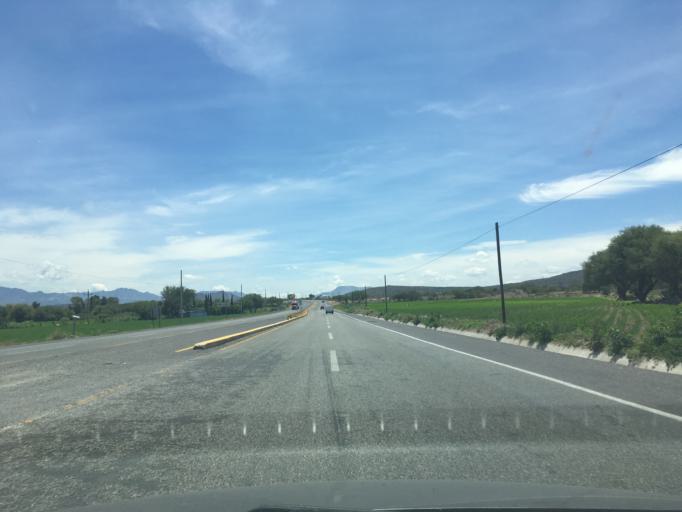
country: MX
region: Hidalgo
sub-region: Alfajayucan
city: Santa Maria Xigui
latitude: 20.4591
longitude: -99.3413
